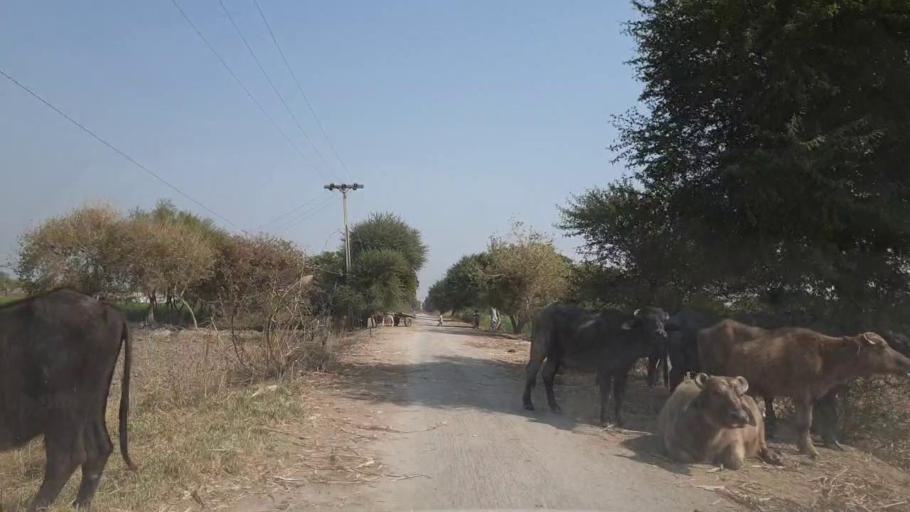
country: PK
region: Sindh
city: Mirpur Khas
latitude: 25.6632
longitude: 69.1746
